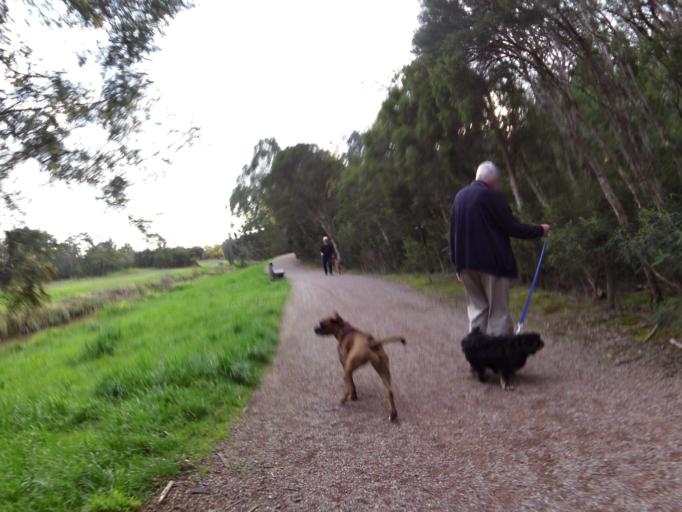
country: AU
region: Victoria
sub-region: Maroondah
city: Heathmont
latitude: -37.8376
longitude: 145.2493
